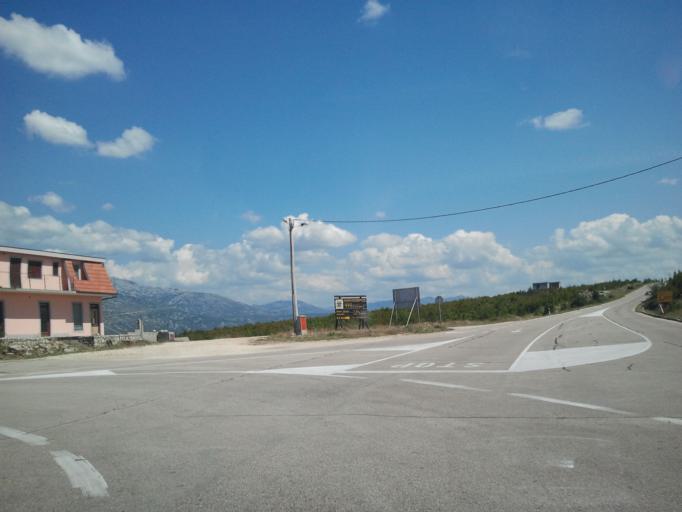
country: HR
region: Zadarska
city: Obrovac
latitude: 44.1946
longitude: 15.6818
